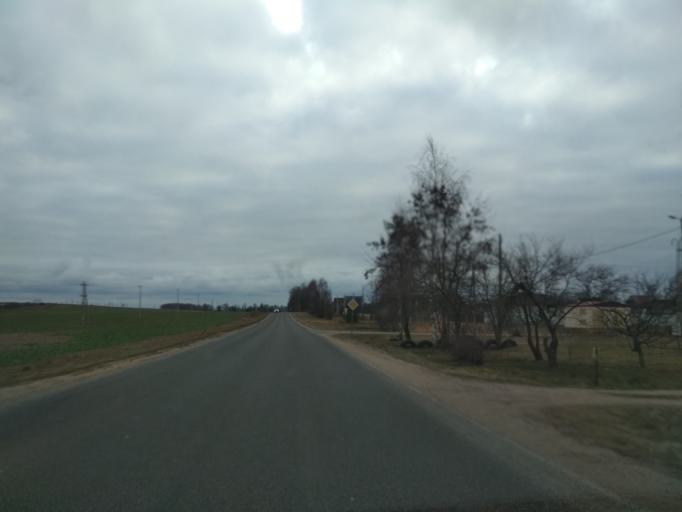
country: BY
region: Minsk
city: Mar''ina Horka
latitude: 53.5415
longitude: 28.1306
